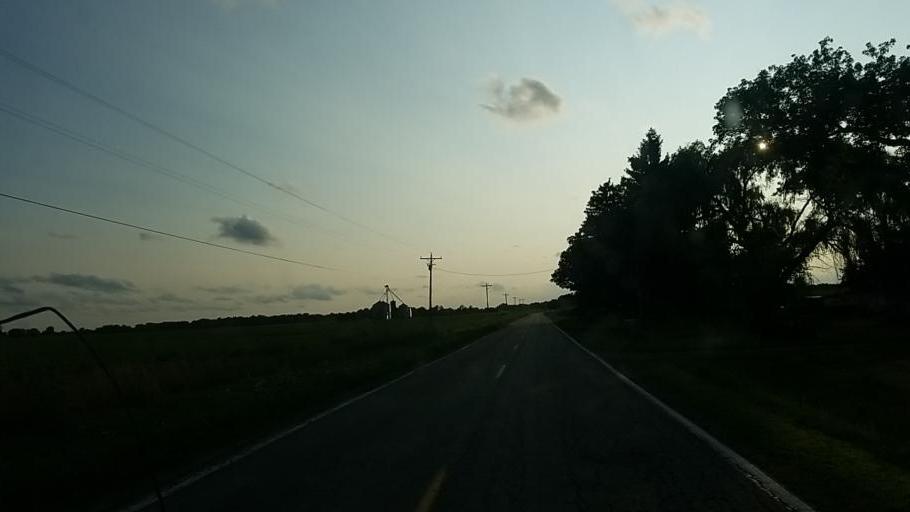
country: US
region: Michigan
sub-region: Montcalm County
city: Howard City
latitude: 43.3593
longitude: -85.3749
